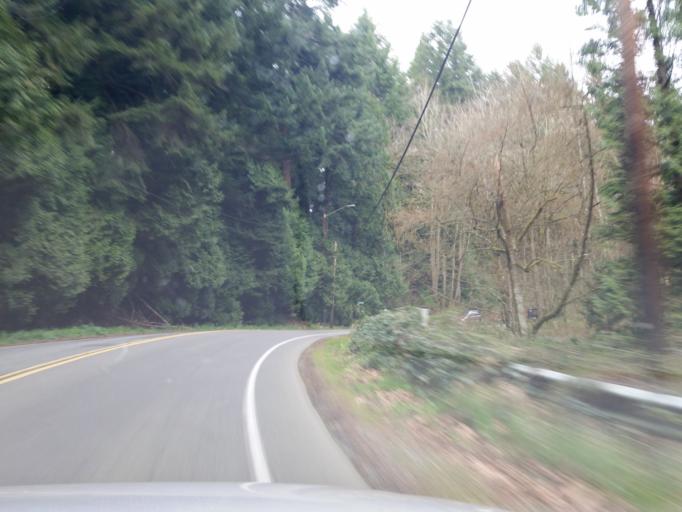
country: US
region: Washington
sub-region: King County
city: Woodinville
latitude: 47.7523
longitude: -122.1439
